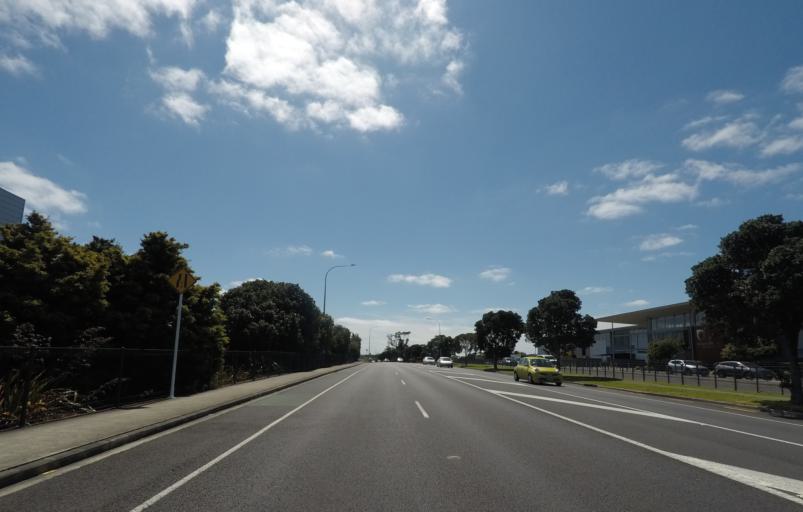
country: NZ
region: Auckland
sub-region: Auckland
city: Pakuranga
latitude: -36.9346
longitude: 174.9149
